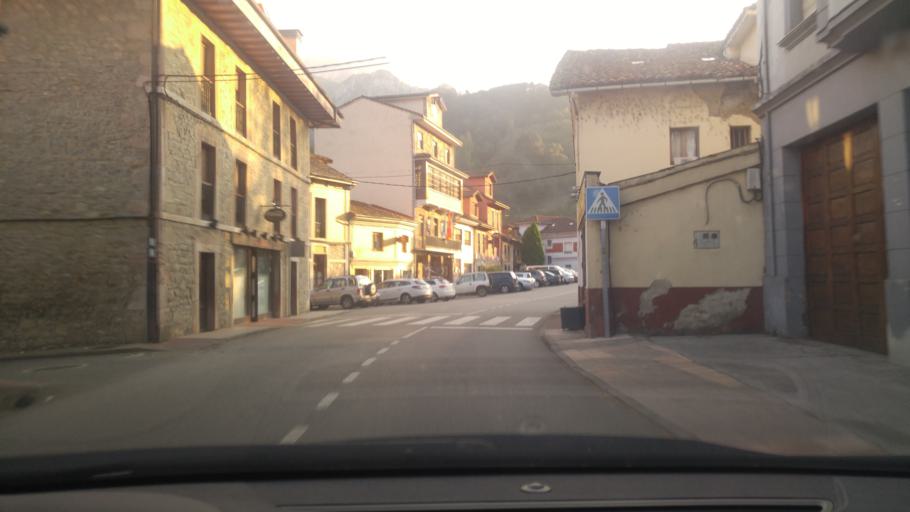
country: ES
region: Asturias
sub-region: Province of Asturias
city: Proaza
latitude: 43.2512
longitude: -6.0166
